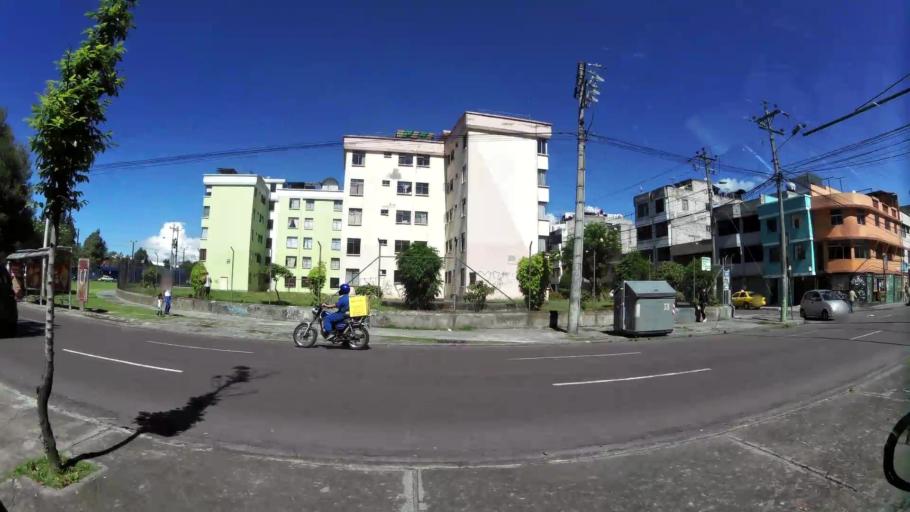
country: EC
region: Pichincha
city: Quito
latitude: -0.2679
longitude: -78.5335
